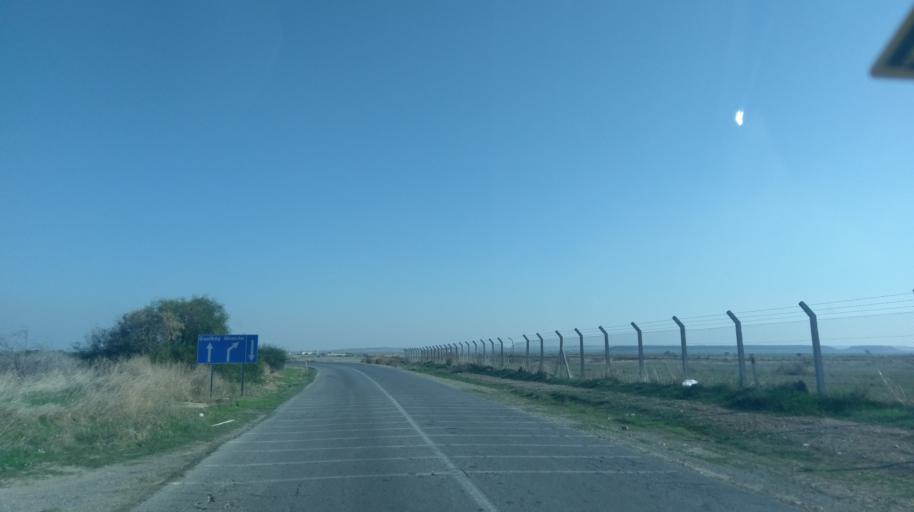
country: CY
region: Larnaka
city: Athienou
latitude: 35.1542
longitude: 33.5144
